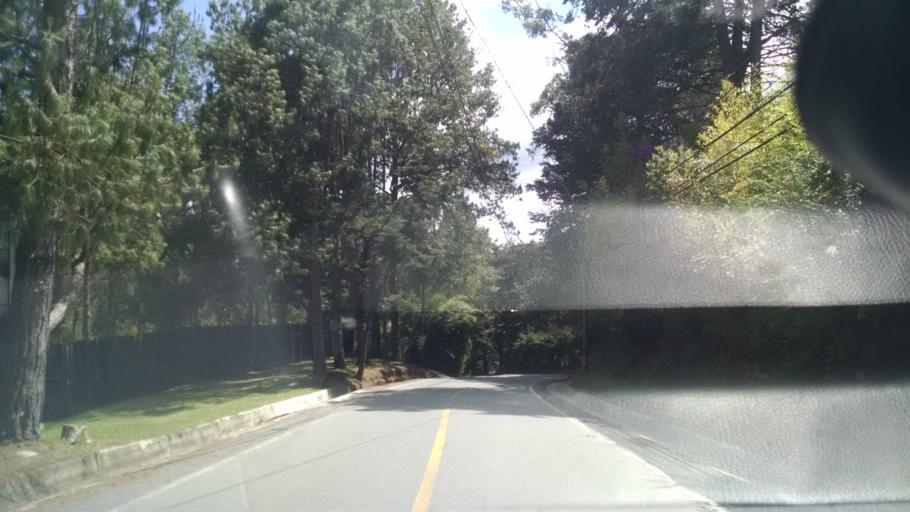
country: CO
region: Antioquia
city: El Retiro
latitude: 6.0924
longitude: -75.5019
